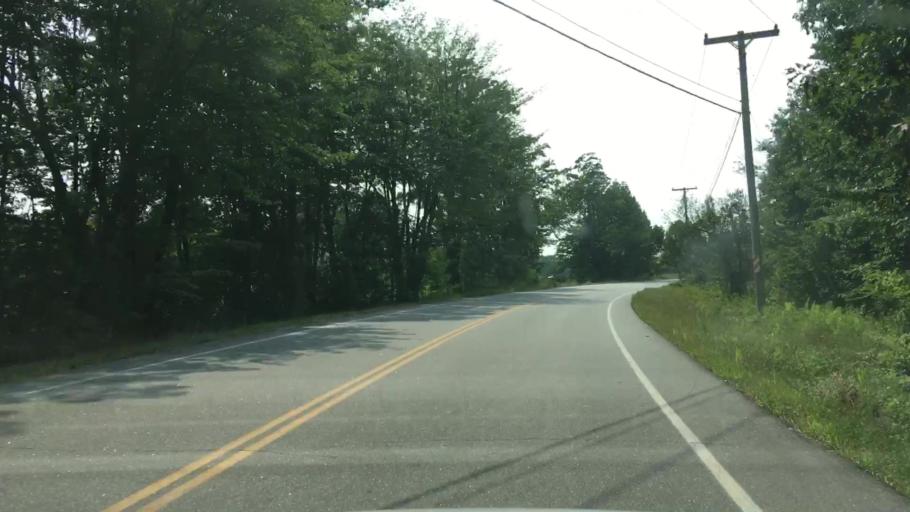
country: US
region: Maine
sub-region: Androscoggin County
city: Livermore
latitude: 44.3293
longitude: -70.2777
